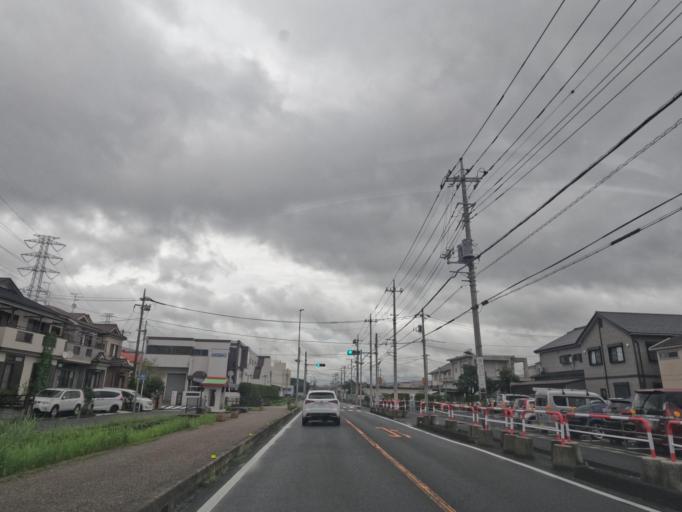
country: JP
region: Saitama
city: Shimotoda
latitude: 35.8485
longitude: 139.6976
